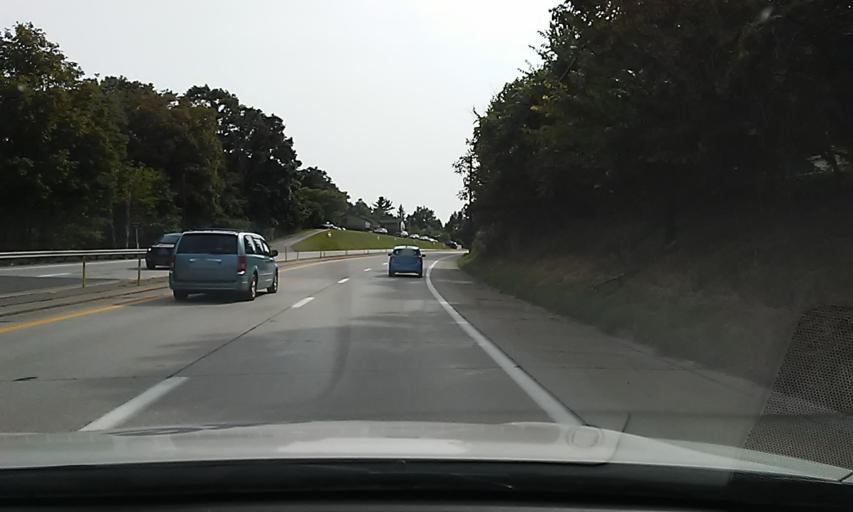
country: US
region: Pennsylvania
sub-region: Fayette County
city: Connellsville
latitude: 40.0401
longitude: -79.5768
